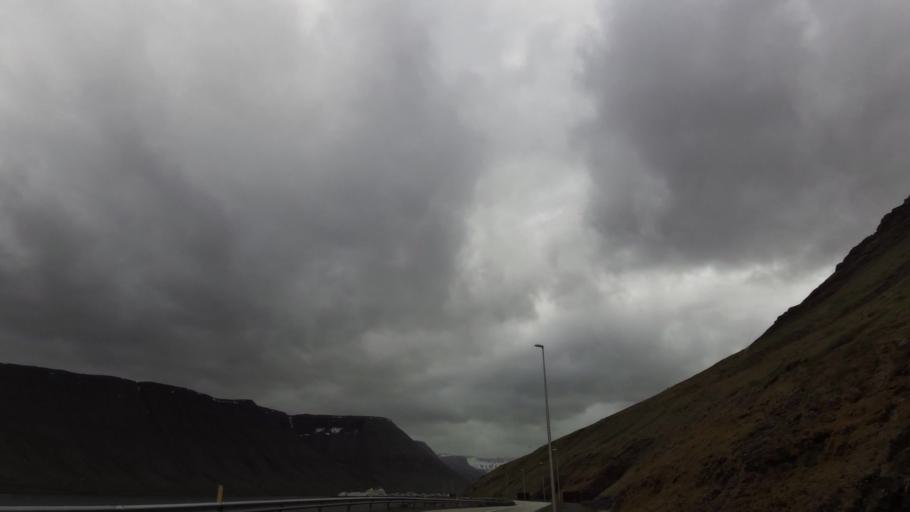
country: IS
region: Westfjords
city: Isafjoerdur
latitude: 66.0960
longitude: -23.1118
